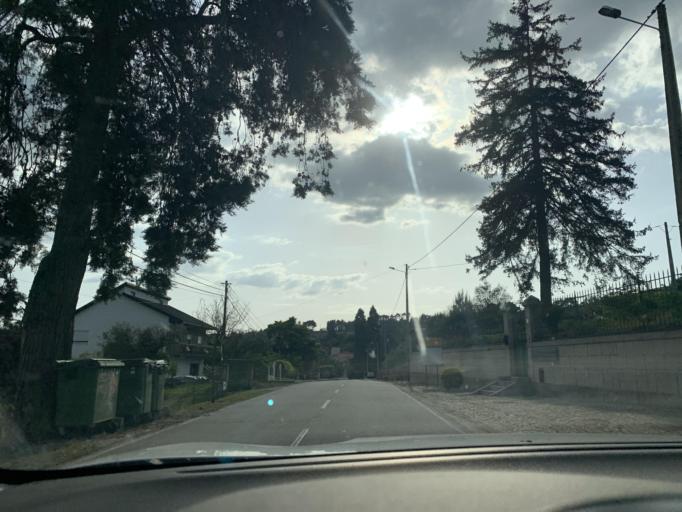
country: PT
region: Guarda
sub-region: Fornos de Algodres
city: Fornos de Algodres
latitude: 40.5802
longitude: -7.6385
